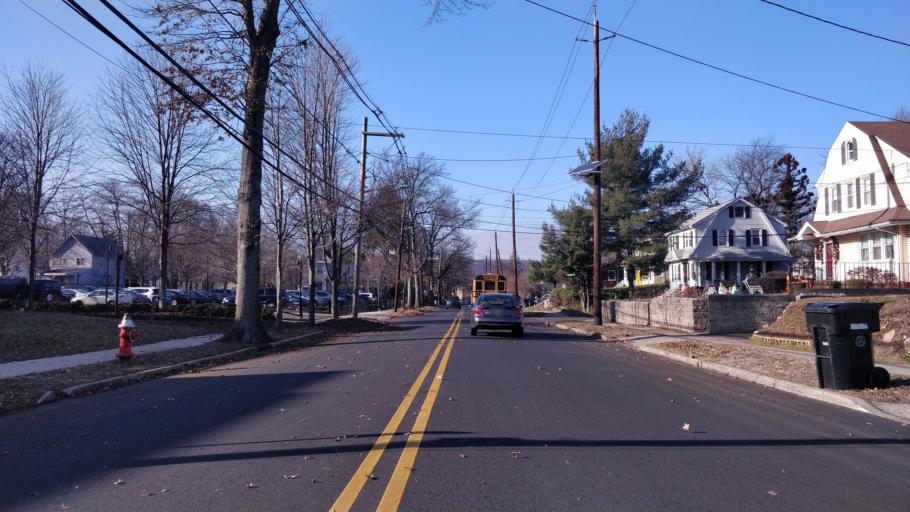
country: US
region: New Jersey
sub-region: Middlesex County
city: Dunellen
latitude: 40.5994
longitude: -74.4414
